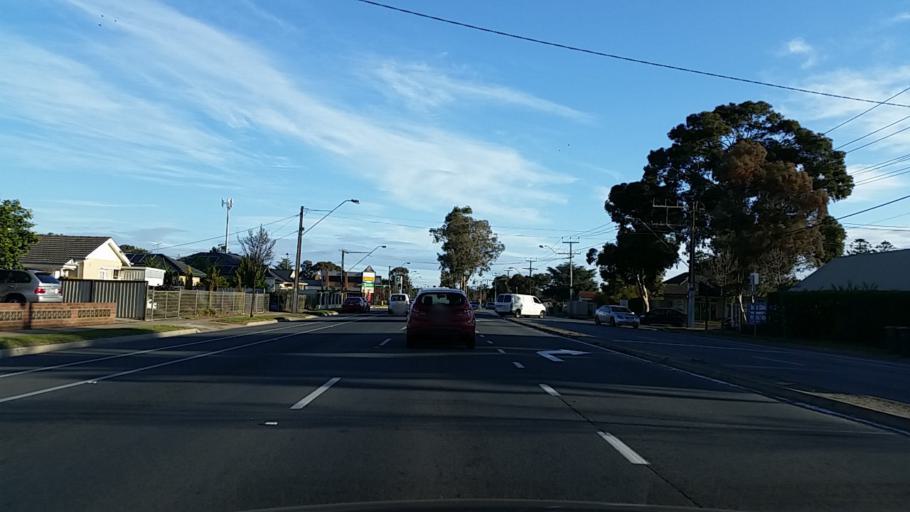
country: AU
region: South Australia
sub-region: Salisbury
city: Salisbury
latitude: -34.7893
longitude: 138.6174
